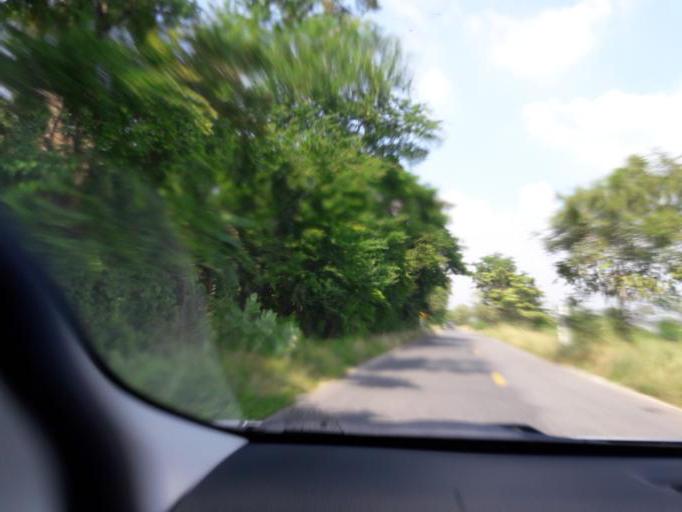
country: TH
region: Ang Thong
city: Ang Thong
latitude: 14.5882
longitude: 100.3994
